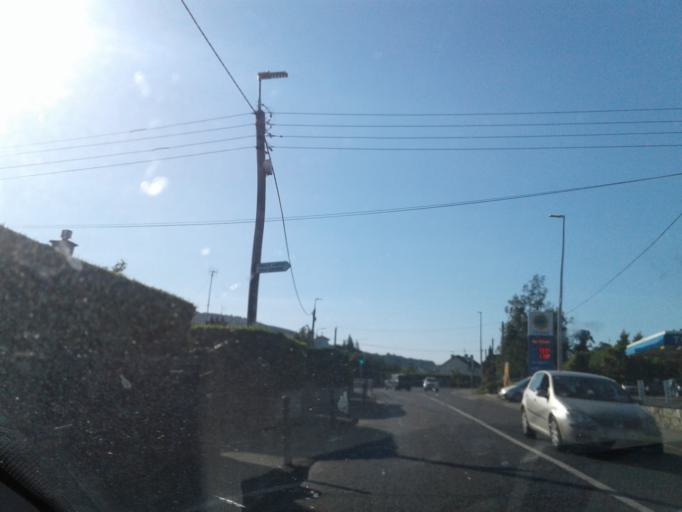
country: IE
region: Leinster
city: Foxrock
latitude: 53.2350
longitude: -6.1925
